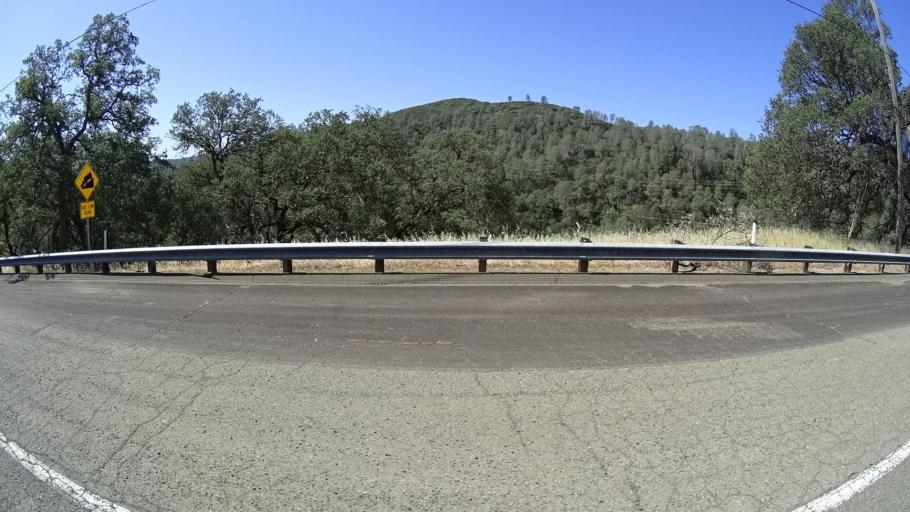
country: US
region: California
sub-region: Lake County
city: Lower Lake
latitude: 38.8892
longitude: -122.5372
